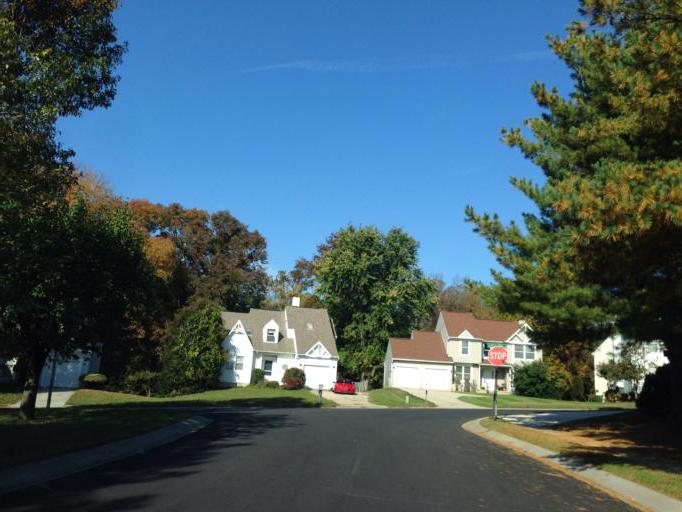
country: US
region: Maryland
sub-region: Howard County
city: Ellicott City
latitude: 39.2733
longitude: -76.8135
